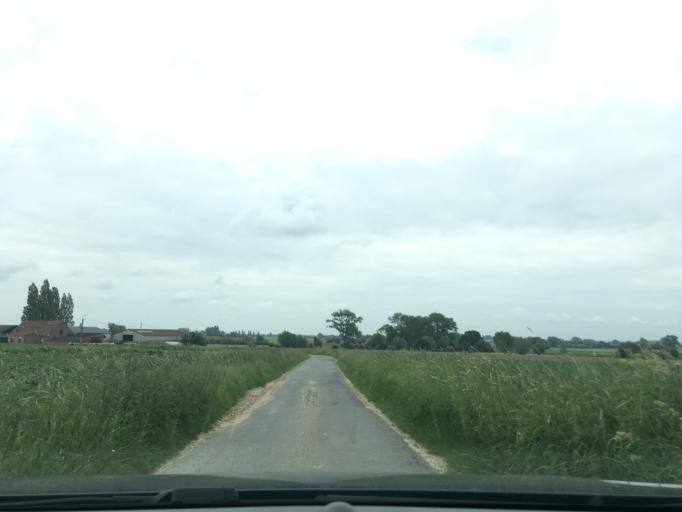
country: BE
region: Flanders
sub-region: Provincie West-Vlaanderen
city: Moorslede
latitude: 50.8929
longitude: 3.0843
